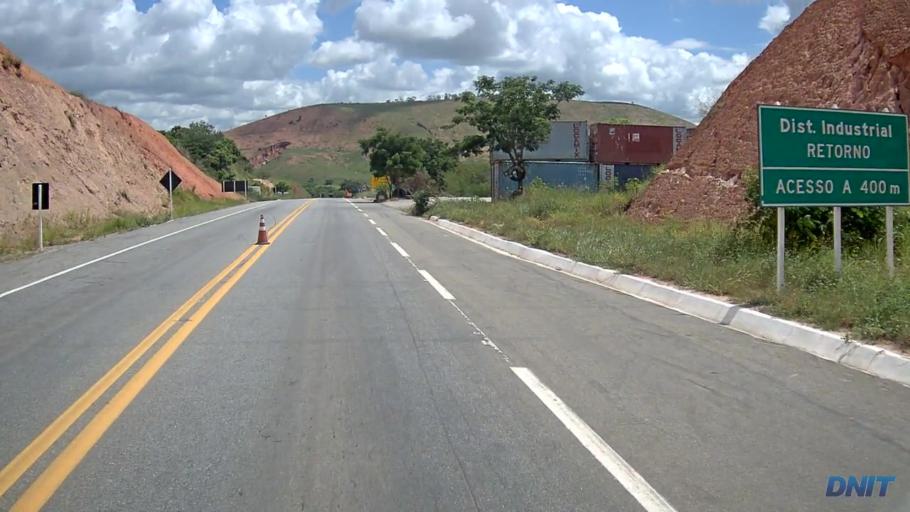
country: BR
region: Minas Gerais
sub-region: Governador Valadares
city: Governador Valadares
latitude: -18.8950
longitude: -42.0046
